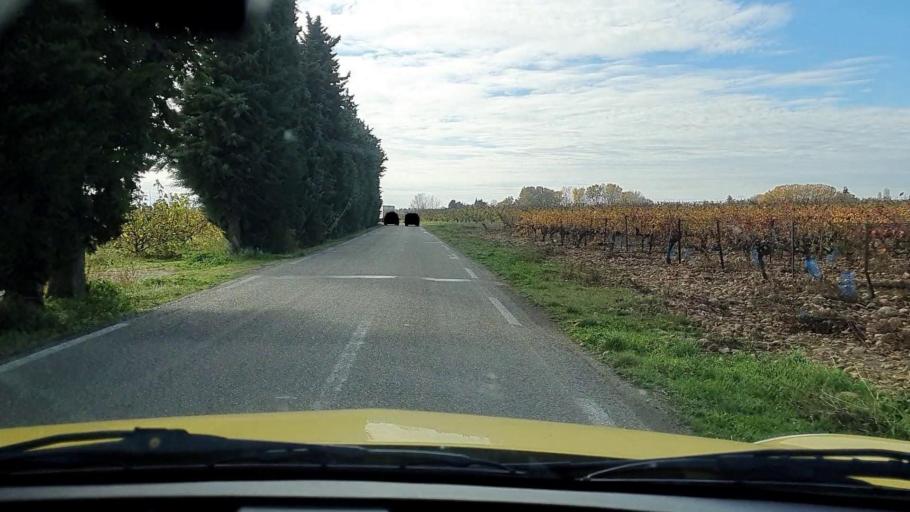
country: FR
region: Languedoc-Roussillon
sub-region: Departement du Gard
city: Jonquieres-Saint-Vincent
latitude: 43.8381
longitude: 4.5677
